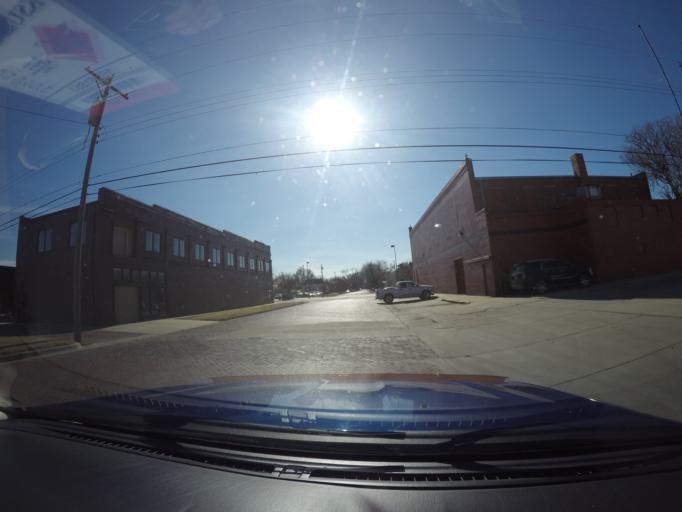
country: US
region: Kansas
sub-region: Sedgwick County
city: Wichita
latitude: 37.6845
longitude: -97.3507
